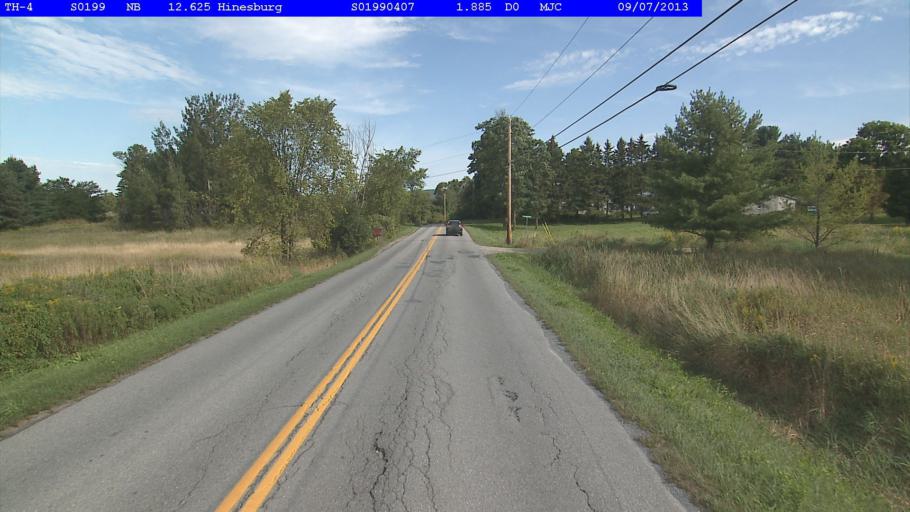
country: US
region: Vermont
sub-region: Chittenden County
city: Hinesburg
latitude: 44.3051
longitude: -73.1089
